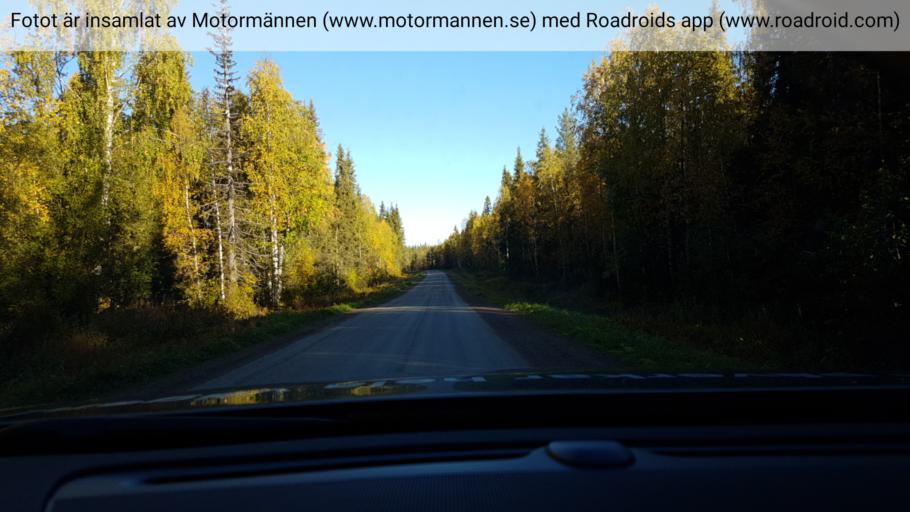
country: SE
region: Norrbotten
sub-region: Alvsbyns Kommun
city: AElvsbyn
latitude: 66.2372
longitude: 21.1581
